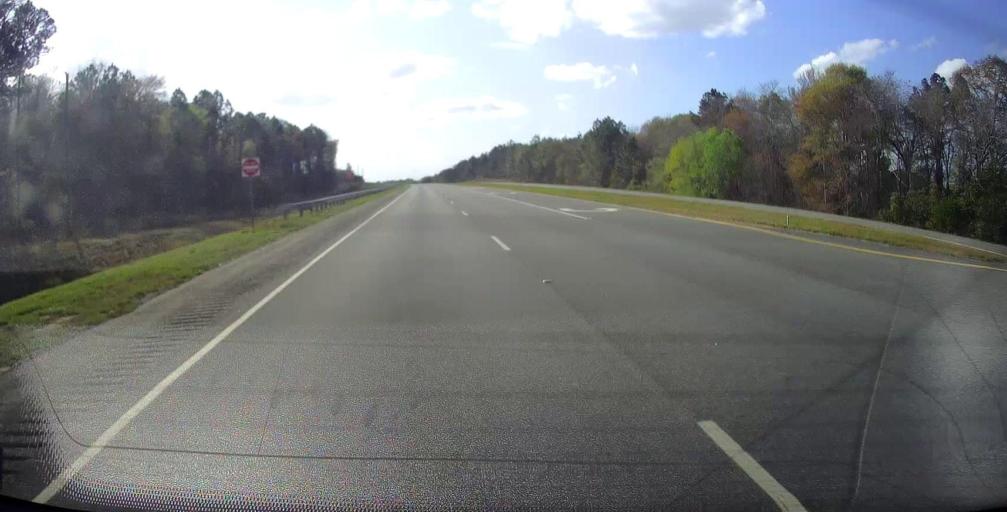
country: US
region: Georgia
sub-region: Telfair County
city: Helena
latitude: 32.1029
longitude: -83.0214
